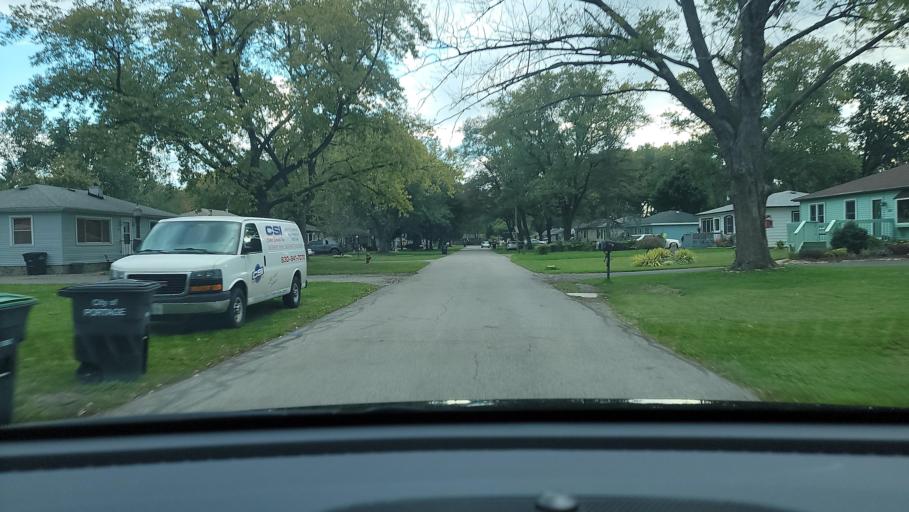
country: US
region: Indiana
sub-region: Porter County
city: Portage
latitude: 41.5706
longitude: -87.1800
